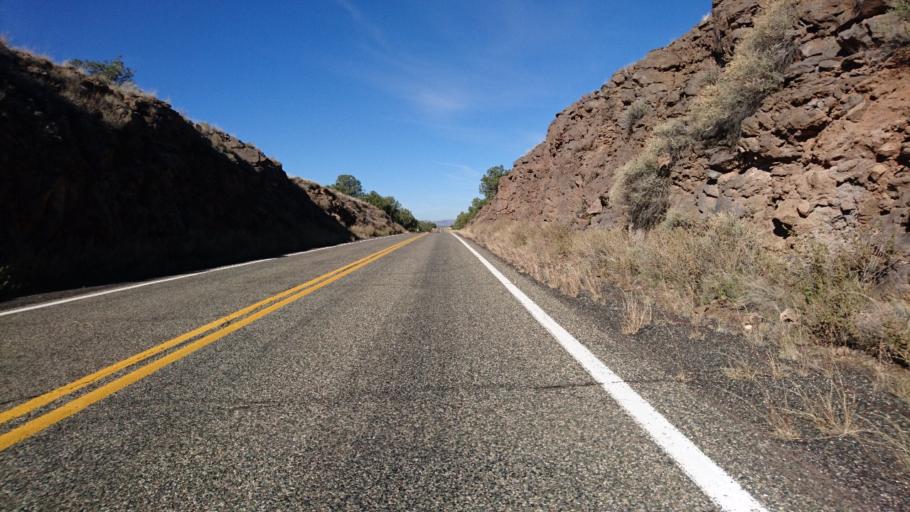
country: US
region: Arizona
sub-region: Yavapai County
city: Paulden
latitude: 35.2801
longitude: -112.7042
